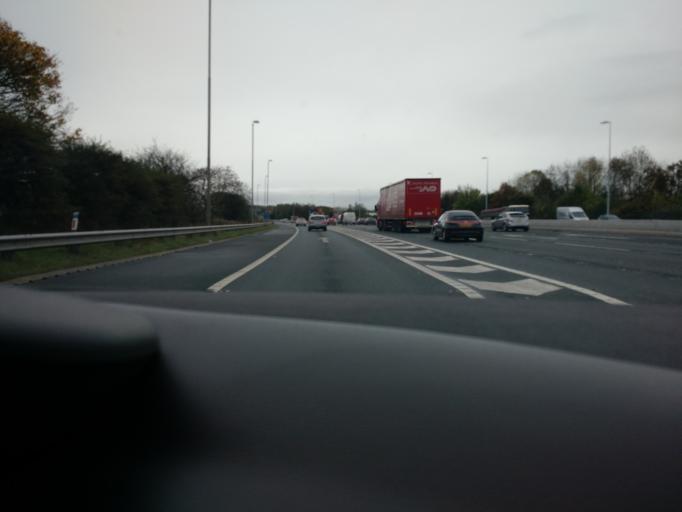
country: GB
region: England
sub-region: Lancashire
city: Goosnargh
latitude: 53.8015
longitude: -2.6912
